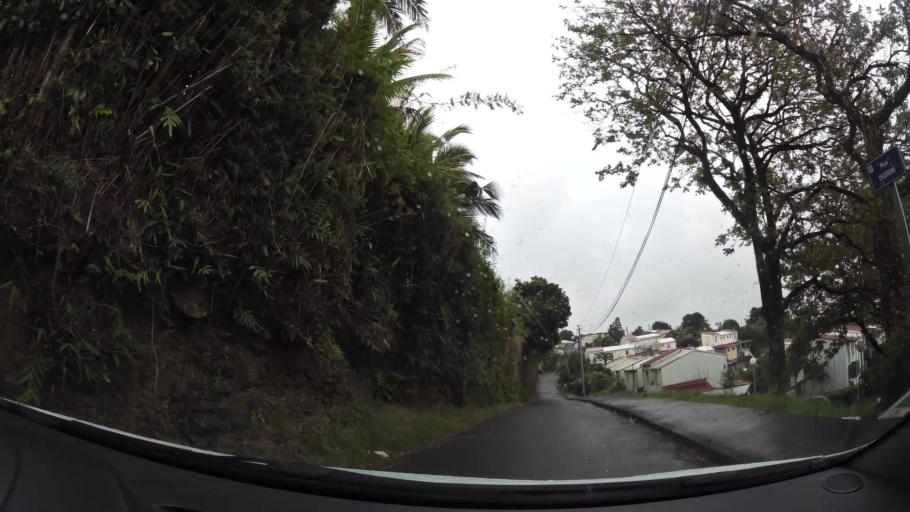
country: RE
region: Reunion
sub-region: Reunion
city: Saint-Andre
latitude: -20.9594
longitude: 55.6460
